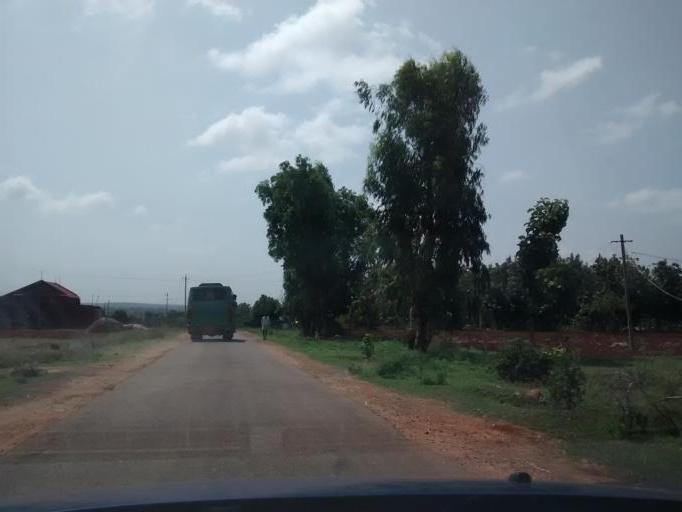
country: IN
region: Karnataka
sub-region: Hassan
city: Hole Narsipur
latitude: 12.7014
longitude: 76.1597
